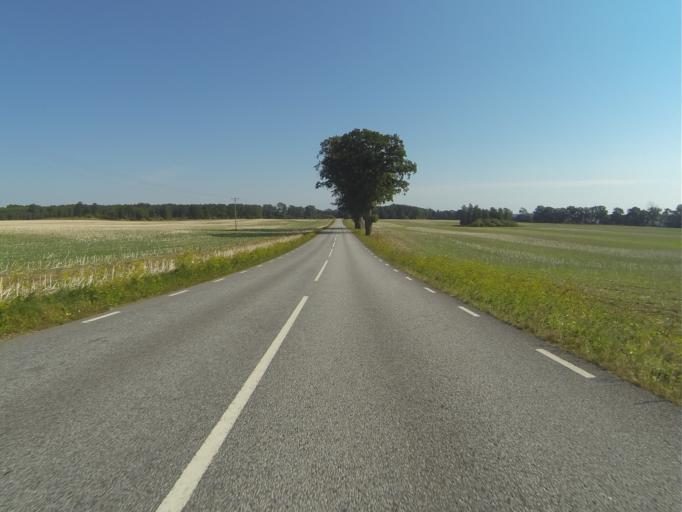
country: SE
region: Skane
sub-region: Sjobo Kommun
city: Blentarp
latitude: 55.6974
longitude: 13.6009
